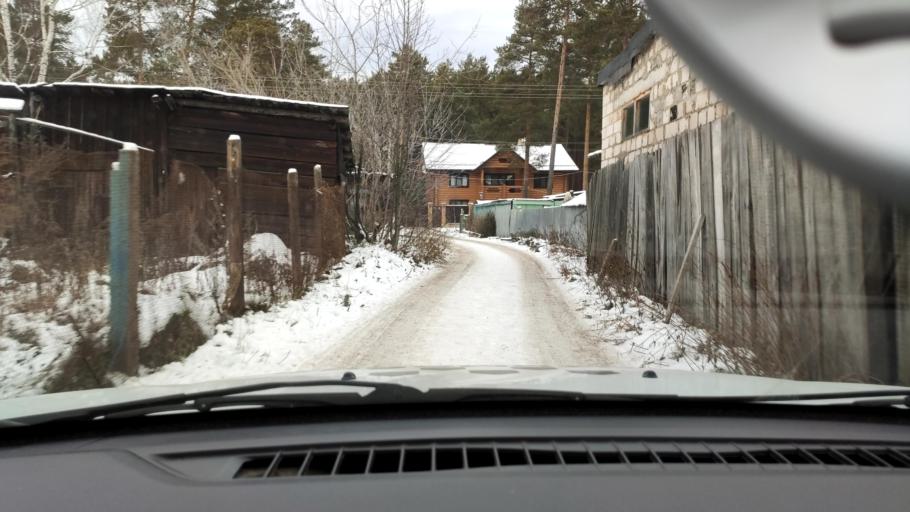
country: RU
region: Perm
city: Perm
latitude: 58.0537
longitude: 56.2851
